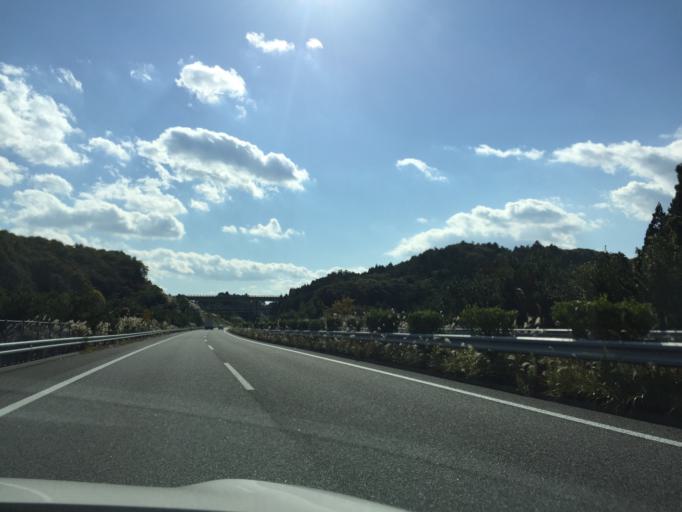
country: JP
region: Fukushima
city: Iwaki
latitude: 37.1939
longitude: 140.9864
